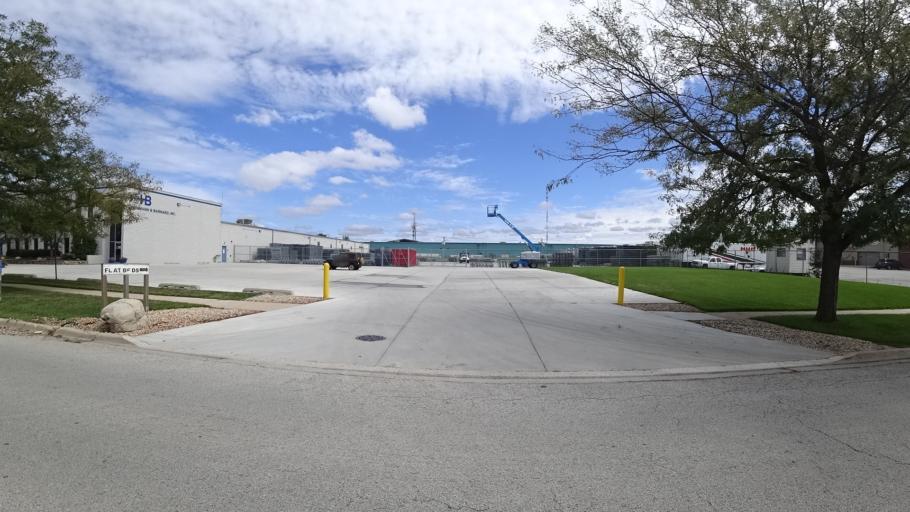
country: US
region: Illinois
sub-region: Cook County
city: Chicago Ridge
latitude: 41.7092
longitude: -87.7919
